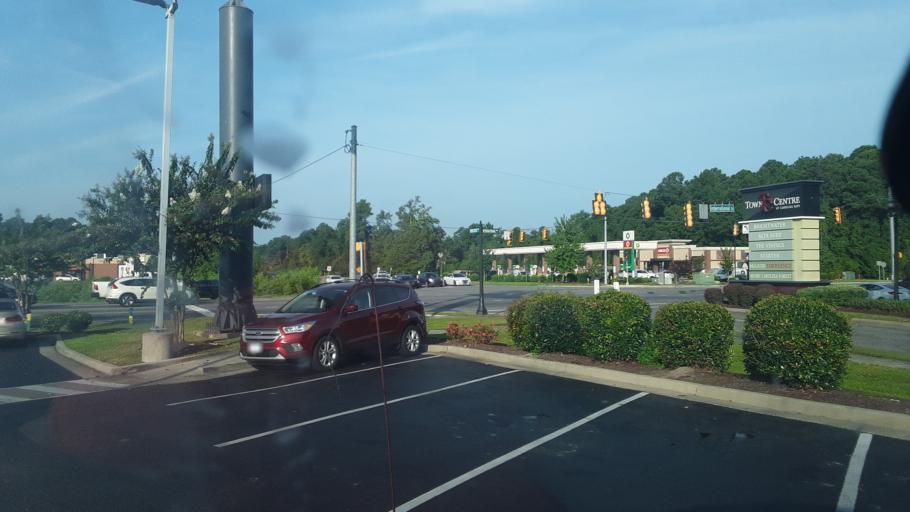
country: US
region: South Carolina
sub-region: Horry County
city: Myrtle Beach
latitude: 33.7606
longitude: -78.8586
